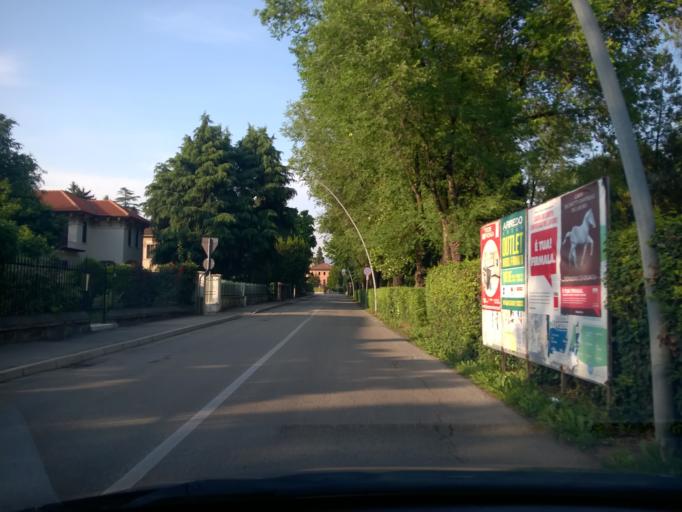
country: IT
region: Veneto
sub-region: Provincia di Vicenza
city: Thiene
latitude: 45.7093
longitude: 11.4848
